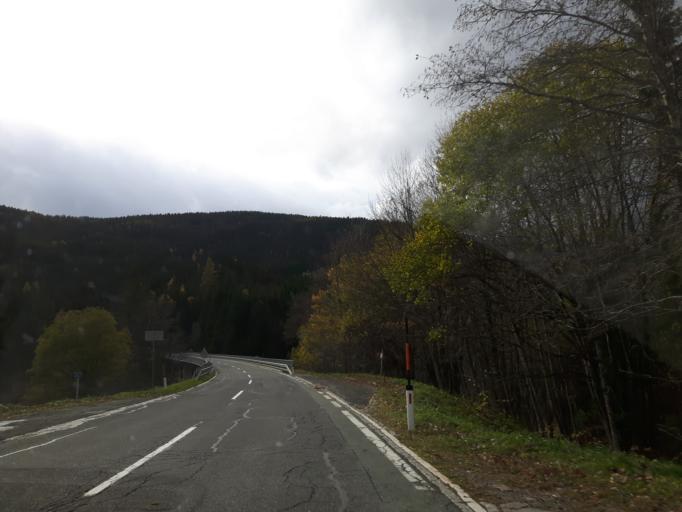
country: AT
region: Styria
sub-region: Politischer Bezirk Deutschlandsberg
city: Soboth
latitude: 46.7009
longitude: 15.0965
